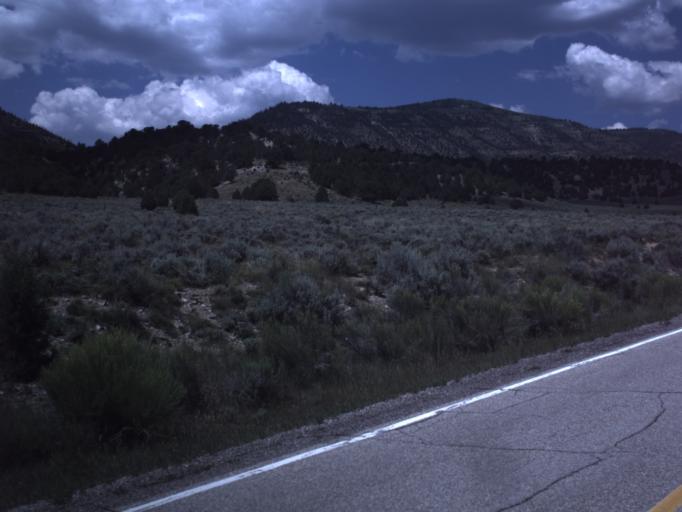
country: US
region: Utah
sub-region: Emery County
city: Orangeville
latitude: 39.3192
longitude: -111.2826
